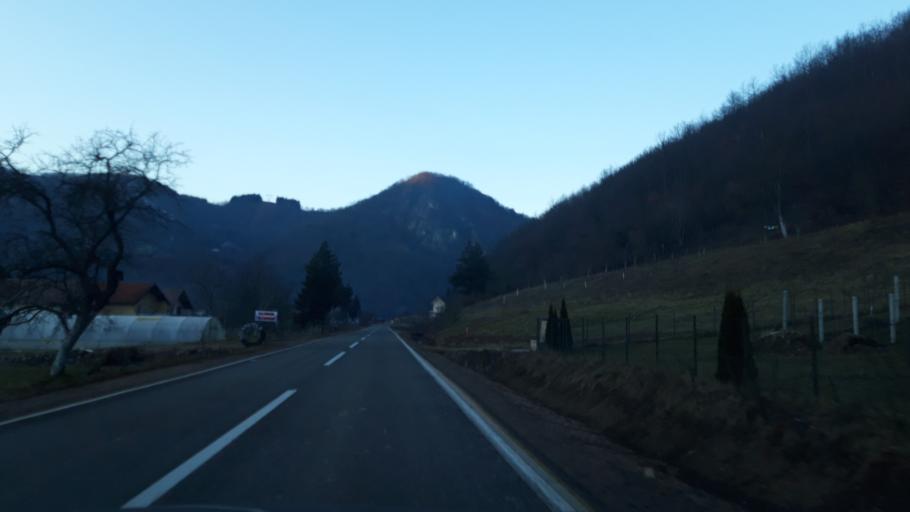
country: BA
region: Republika Srpska
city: Milici
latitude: 44.2591
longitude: 19.1063
